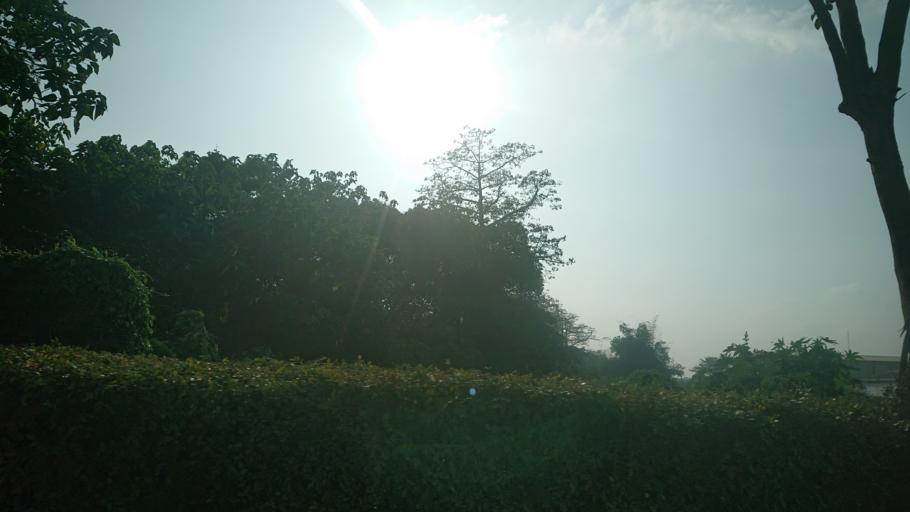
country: TW
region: Taiwan
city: Xinying
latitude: 23.1884
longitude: 120.2717
